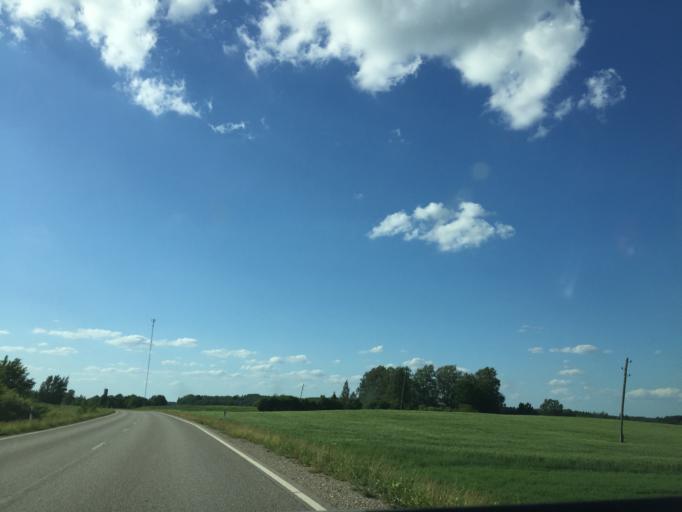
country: LV
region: Kandava
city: Kandava
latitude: 56.9218
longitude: 22.8204
